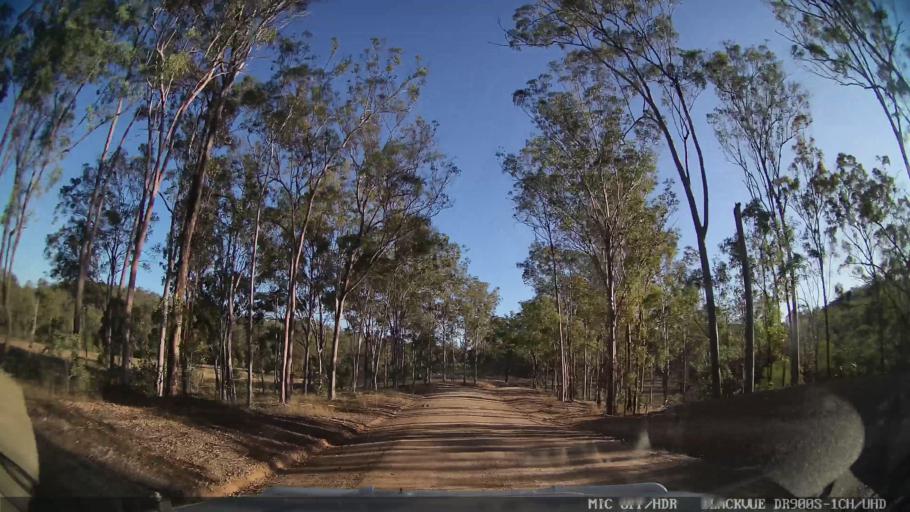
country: AU
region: Queensland
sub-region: Gladstone
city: Toolooa
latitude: -24.6940
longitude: 151.4127
